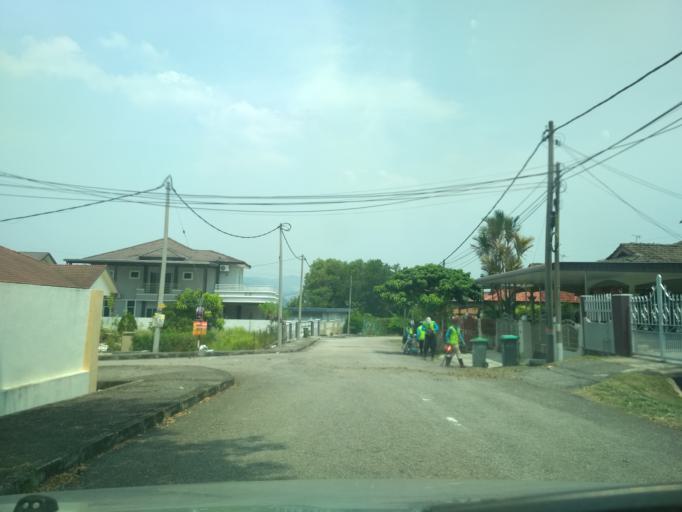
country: MY
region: Kedah
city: Kulim
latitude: 5.3601
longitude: 100.5321
